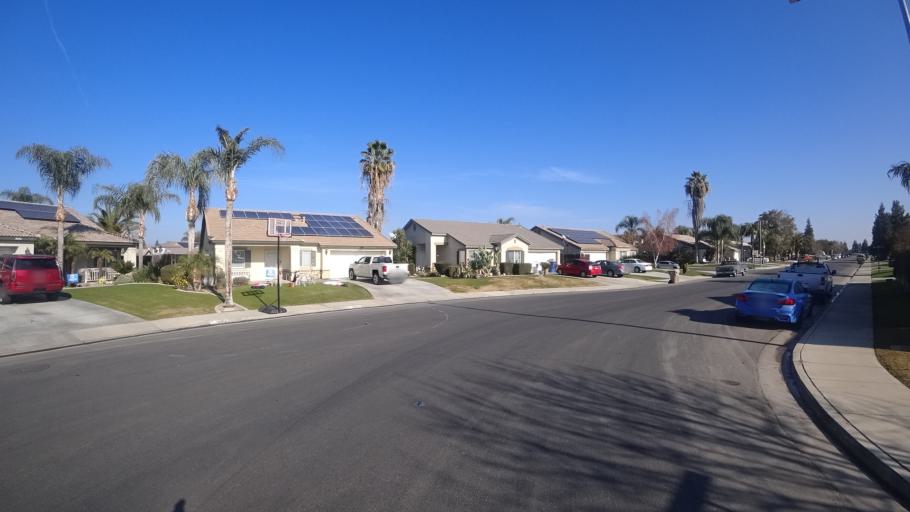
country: US
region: California
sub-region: Kern County
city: Greenacres
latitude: 35.3146
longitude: -119.1229
